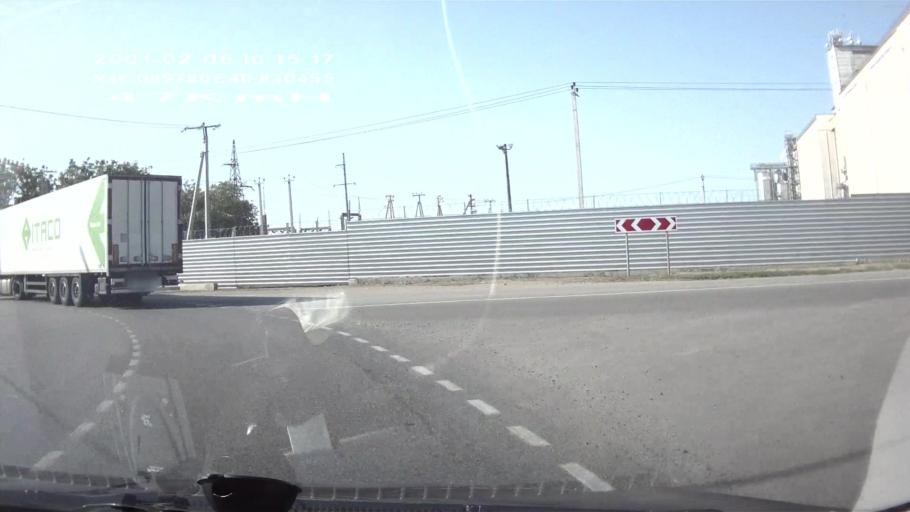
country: RU
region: Krasnodarskiy
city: Belaya Glina
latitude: 46.0897
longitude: 40.8303
